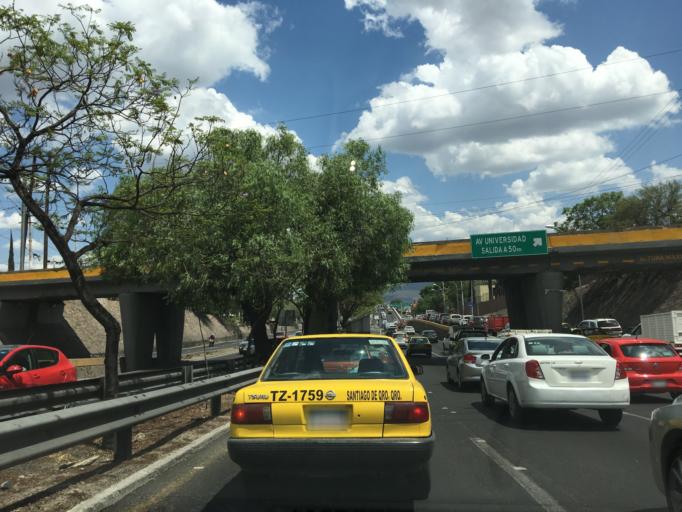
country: MX
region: Queretaro
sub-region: Queretaro
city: Santiago de Queretaro
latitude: 20.6040
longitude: -100.3771
